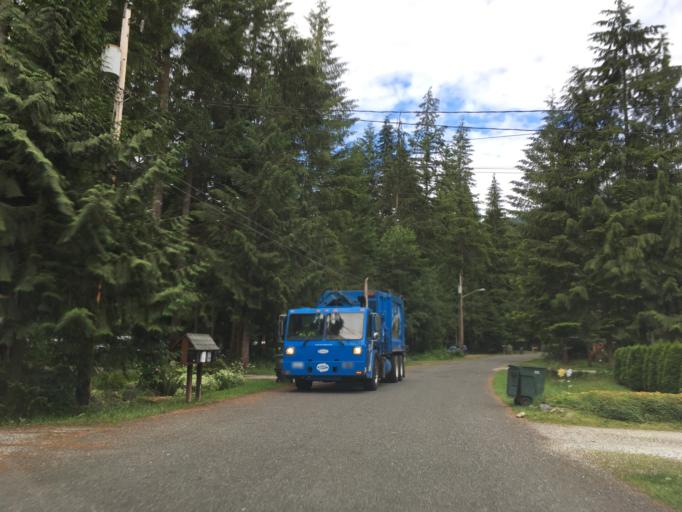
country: US
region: Washington
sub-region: Whatcom County
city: Peaceful Valley
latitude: 48.9399
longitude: -122.1389
